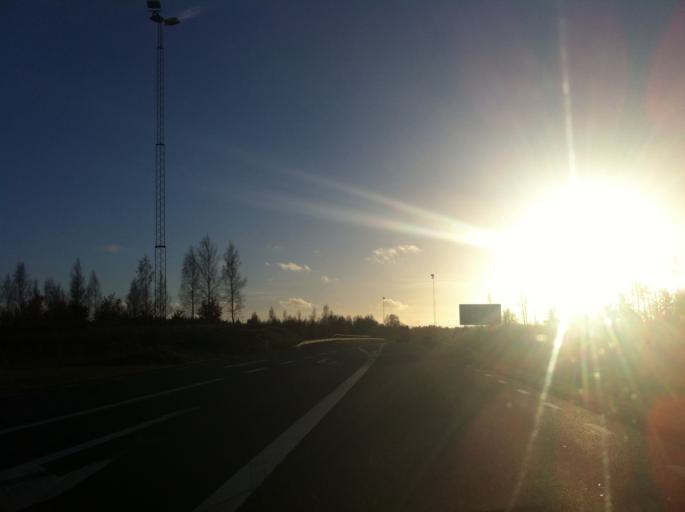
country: SE
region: Skane
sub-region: Hassleholms Kommun
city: Hastveda
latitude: 56.1900
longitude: 13.8960
